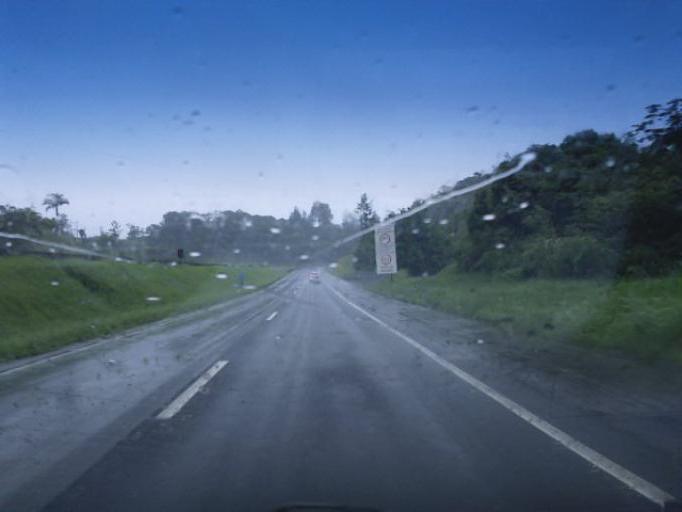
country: BR
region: Sao Paulo
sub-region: Juquia
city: Juquia
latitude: -24.4016
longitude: -47.7376
